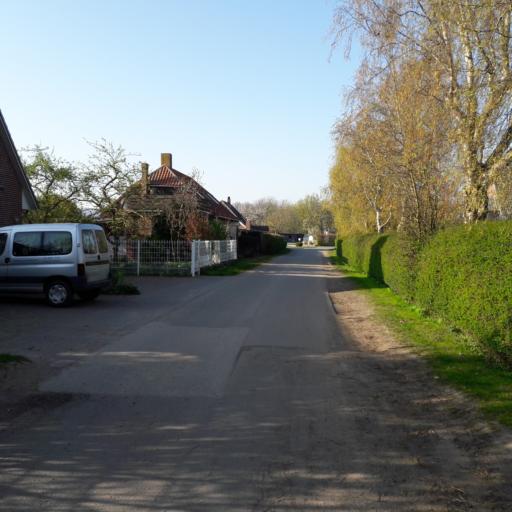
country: DE
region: Schleswig-Holstein
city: Burg auf Fehmarn
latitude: 54.4256
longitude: 11.2260
